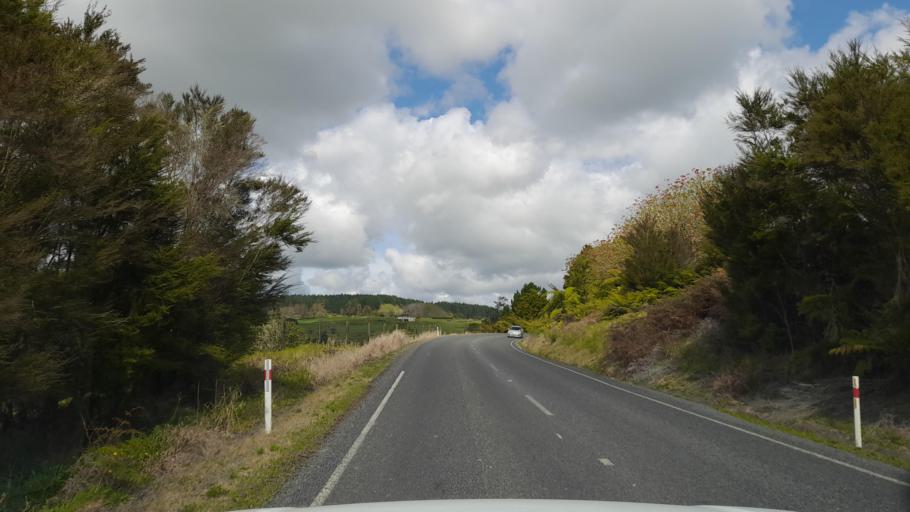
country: NZ
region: Northland
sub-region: Whangarei
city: Maungatapere
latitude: -35.6360
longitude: 174.1095
